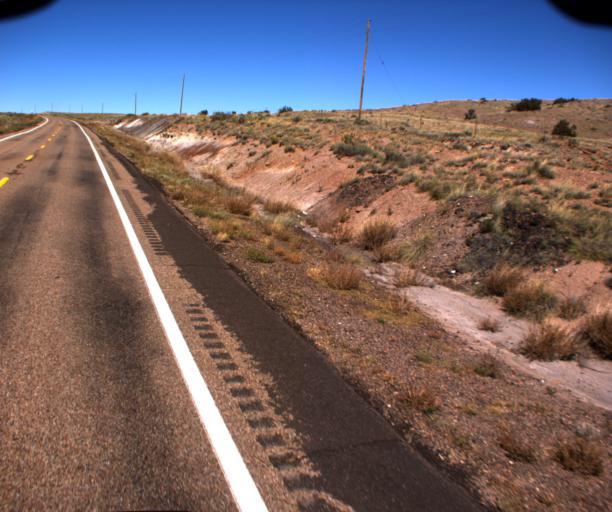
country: US
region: Arizona
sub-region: Apache County
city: Saint Johns
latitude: 34.5269
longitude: -109.4570
